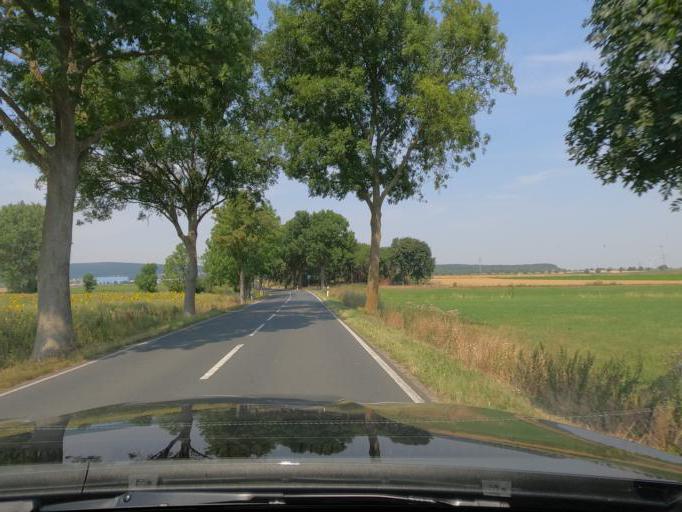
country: DE
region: Lower Saxony
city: Springe
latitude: 52.1971
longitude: 9.6357
